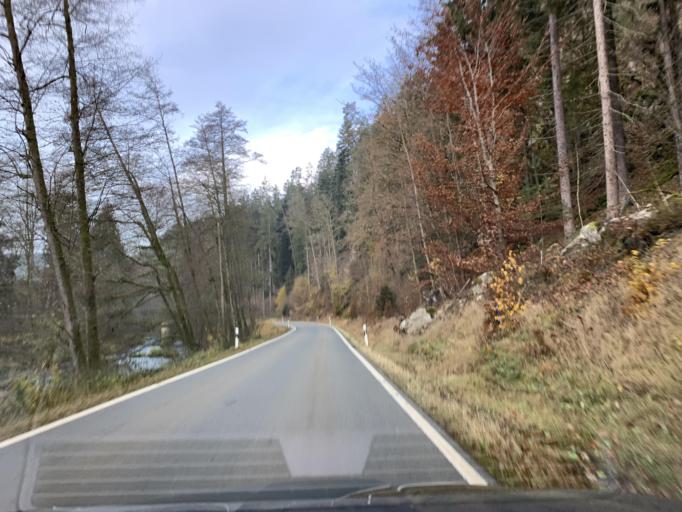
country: DE
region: Bavaria
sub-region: Upper Palatinate
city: Thanstein
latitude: 49.3626
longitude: 12.4438
